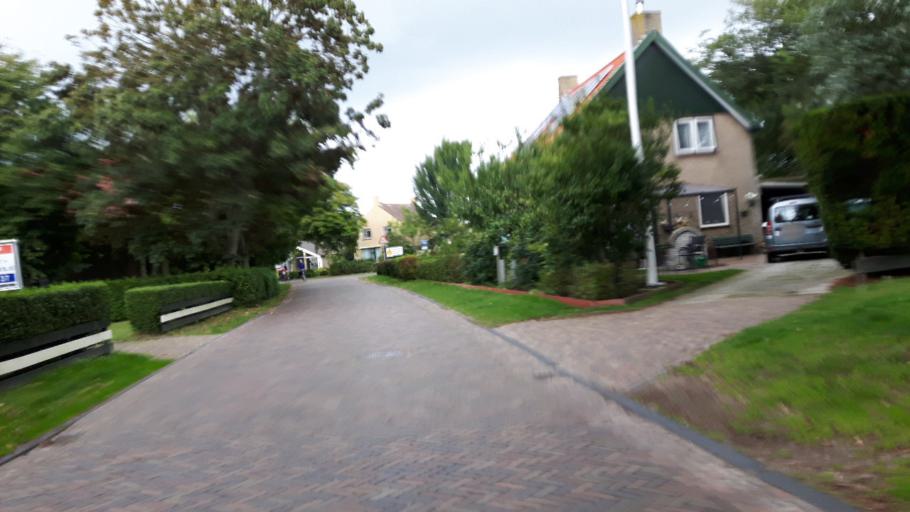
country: NL
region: Friesland
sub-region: Gemeente Ameland
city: Hollum
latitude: 53.4416
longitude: 5.6375
